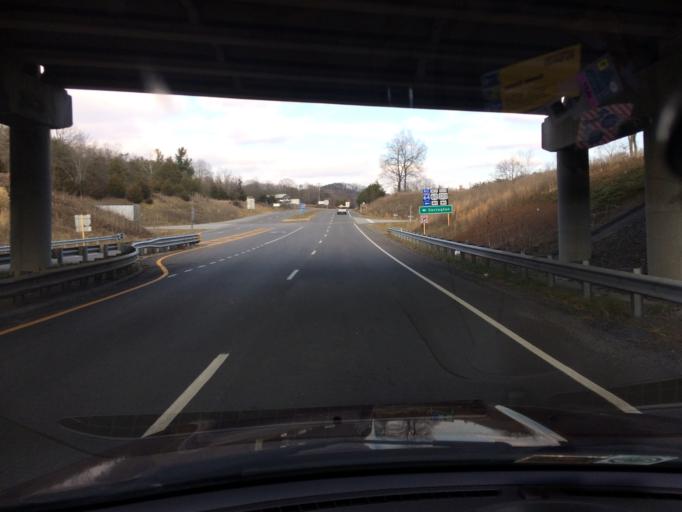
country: US
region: Virginia
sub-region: Alleghany County
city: Clifton Forge
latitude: 37.8271
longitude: -79.7928
